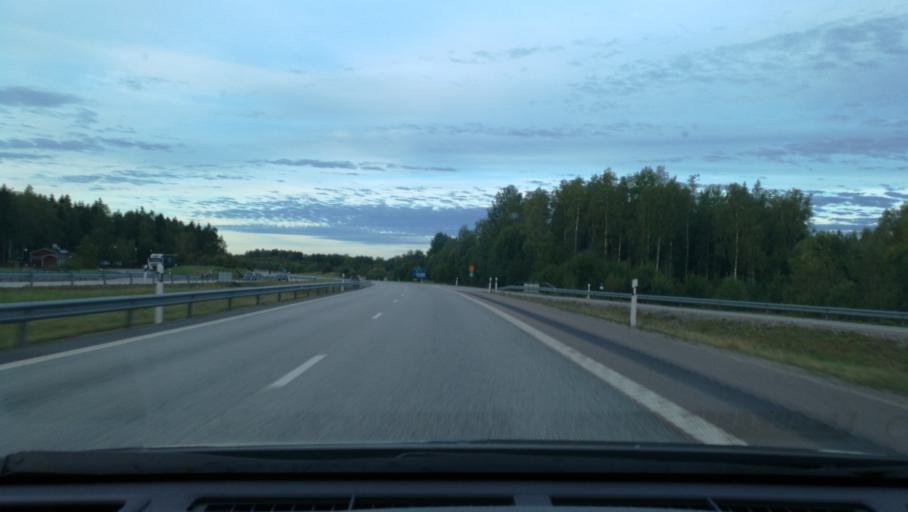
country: SE
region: Vaestmanland
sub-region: Kopings Kommun
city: Koping
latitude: 59.5125
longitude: 15.9455
